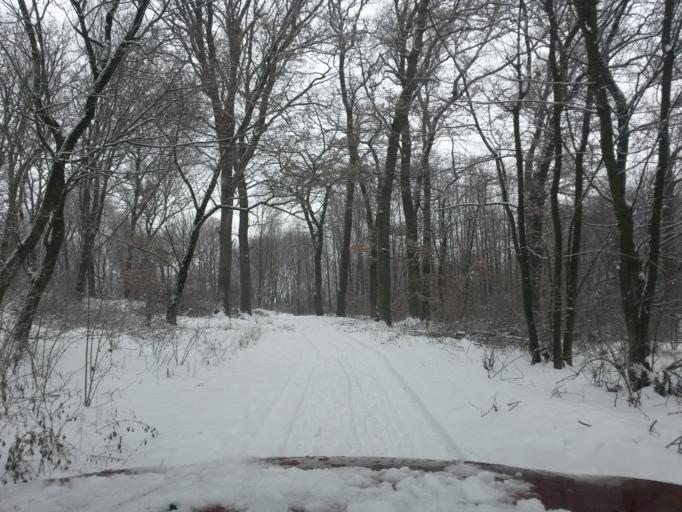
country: SK
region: Kosicky
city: Kosice
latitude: 48.7159
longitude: 21.3291
